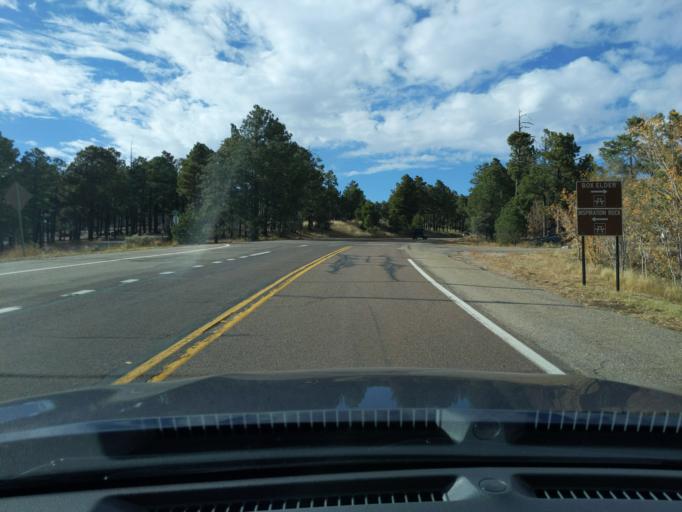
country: US
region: Arizona
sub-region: Pinal County
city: Oracle
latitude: 32.4329
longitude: -110.7505
